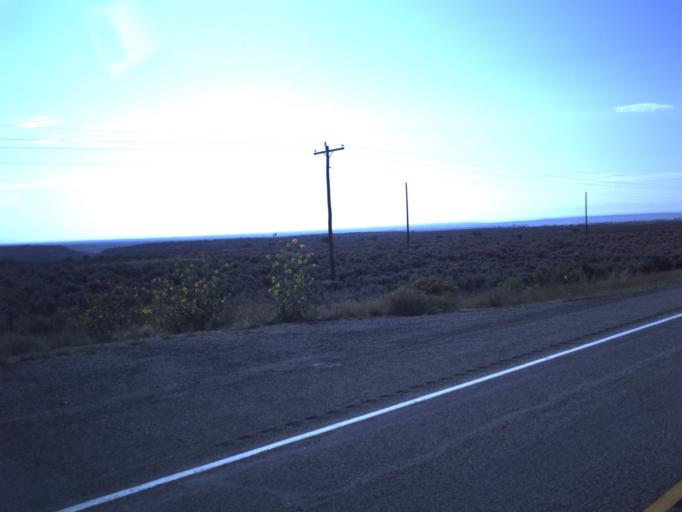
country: US
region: Utah
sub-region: San Juan County
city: Blanding
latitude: 37.5195
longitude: -109.4941
